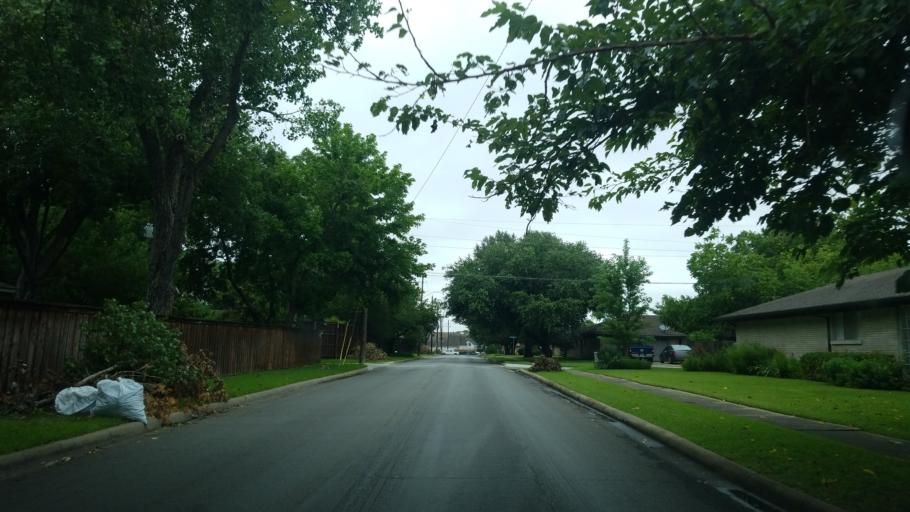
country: US
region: Texas
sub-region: Dallas County
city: Farmers Branch
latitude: 32.8932
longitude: -96.8730
